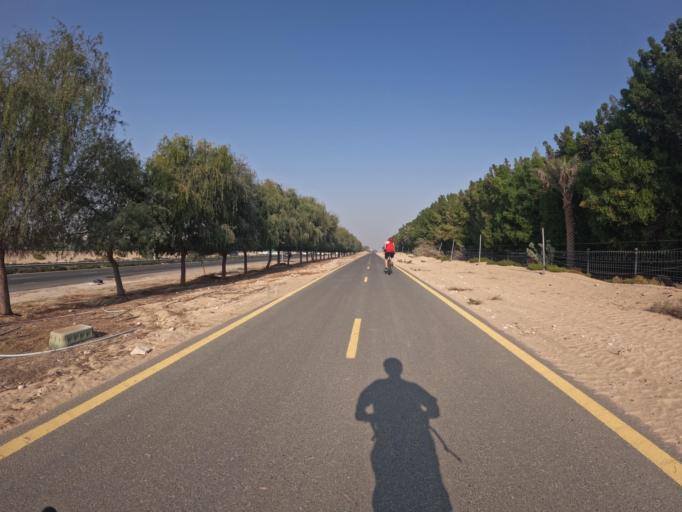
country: AE
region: Dubai
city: Dubai
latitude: 25.0092
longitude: 55.2950
